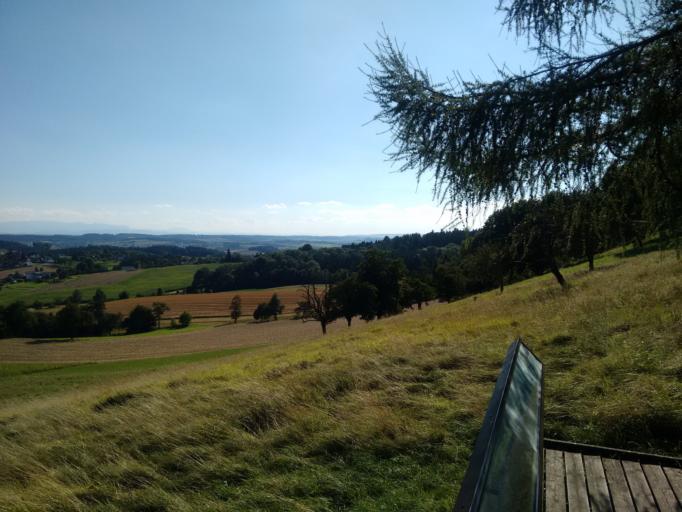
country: AT
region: Upper Austria
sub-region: Wels-Land
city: Buchkirchen
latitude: 48.2394
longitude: 14.0146
